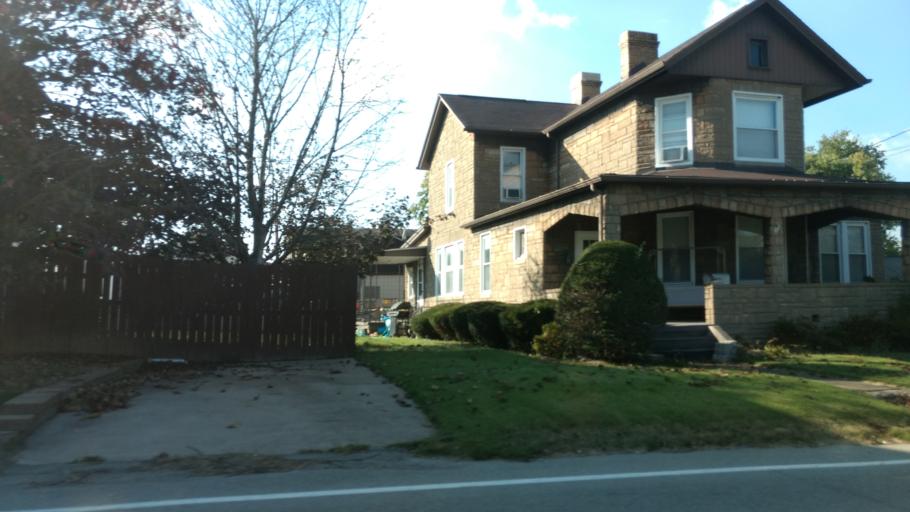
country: US
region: Pennsylvania
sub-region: Westmoreland County
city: Lynnwood-Pricedale
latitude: 40.1298
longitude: -79.8450
